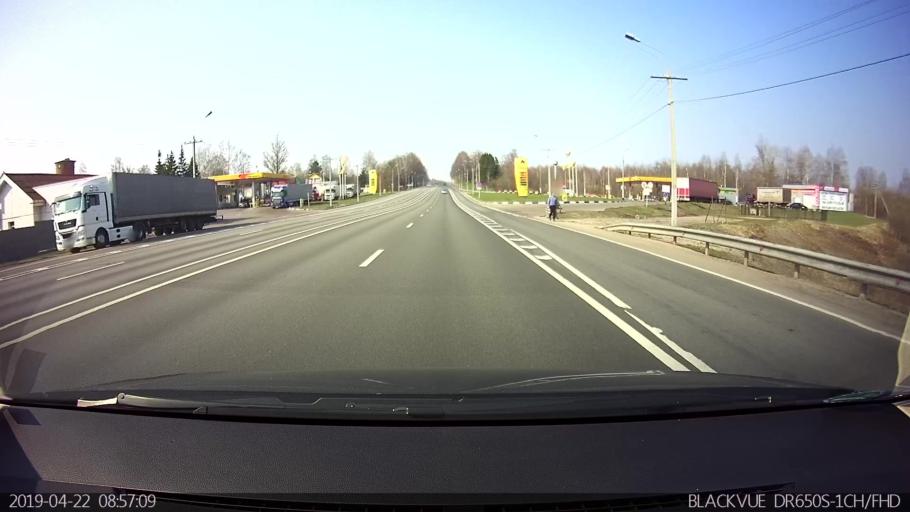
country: RU
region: Smolensk
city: Pechersk
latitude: 54.8703
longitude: 32.0225
